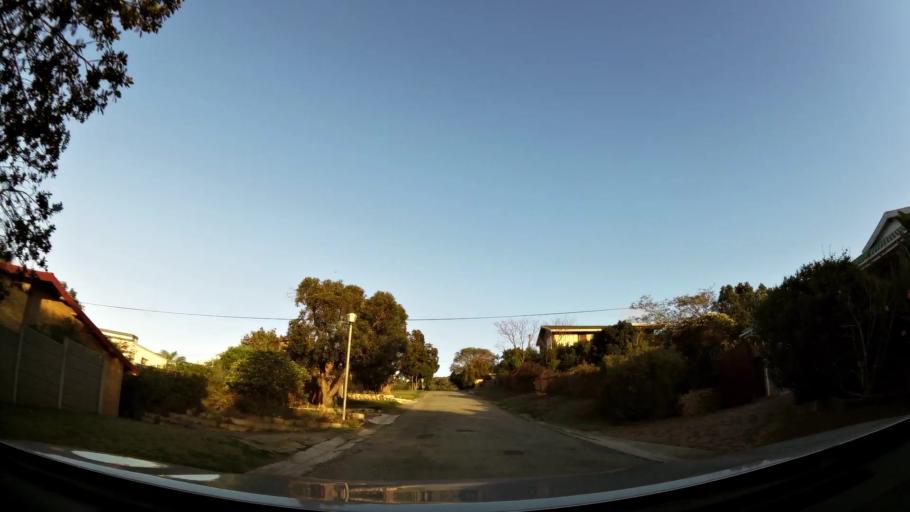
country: ZA
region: Western Cape
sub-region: Eden District Municipality
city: Knysna
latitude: -34.0211
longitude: 22.8128
